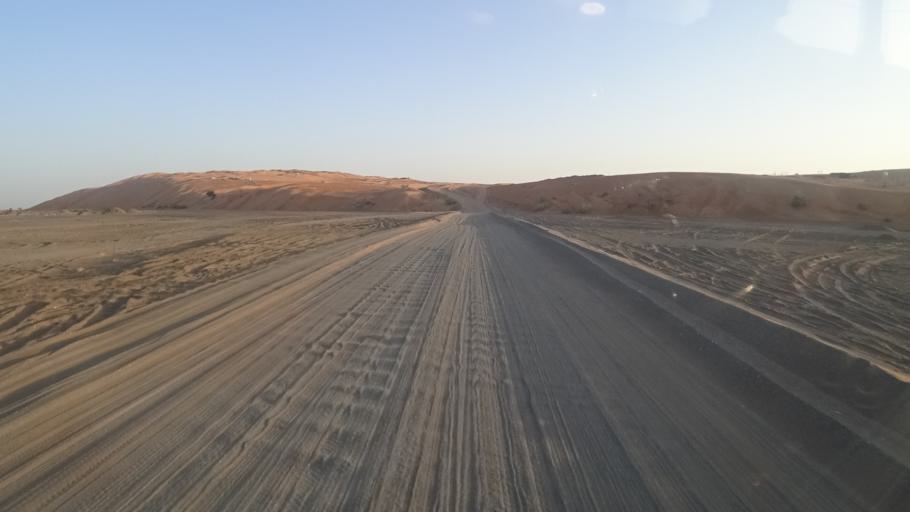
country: OM
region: Ash Sharqiyah
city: Badiyah
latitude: 22.4918
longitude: 58.7293
